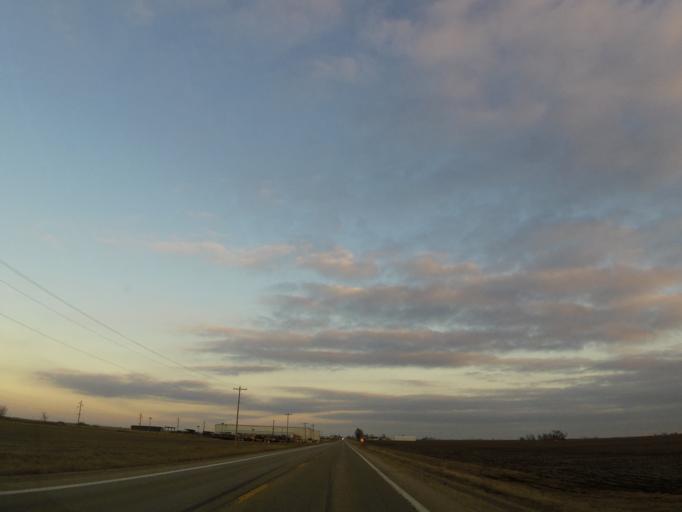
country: US
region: Illinois
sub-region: Woodford County
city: El Paso
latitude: 40.7380
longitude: -88.9820
